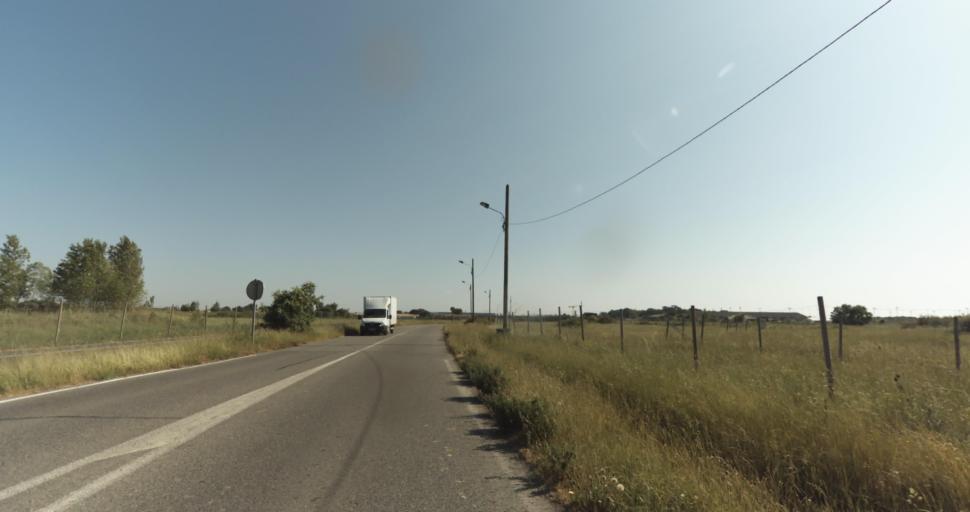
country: FR
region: Midi-Pyrenees
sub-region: Departement de la Haute-Garonne
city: La Salvetat-Saint-Gilles
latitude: 43.5854
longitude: 1.2890
